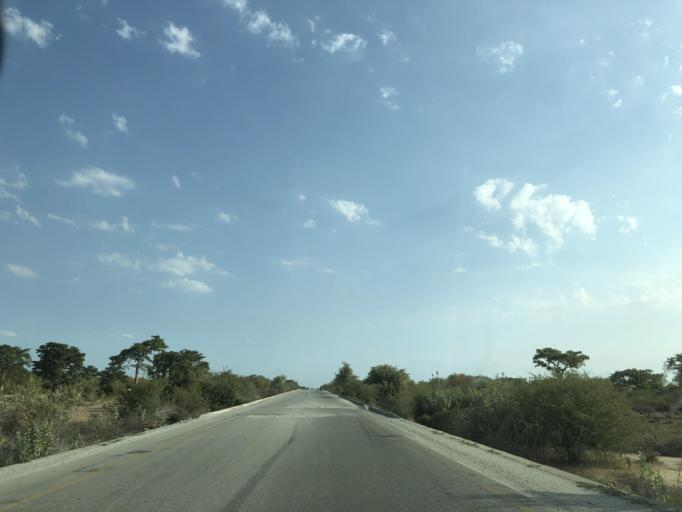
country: AO
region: Benguela
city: Benguela
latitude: -13.1903
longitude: 13.7623
